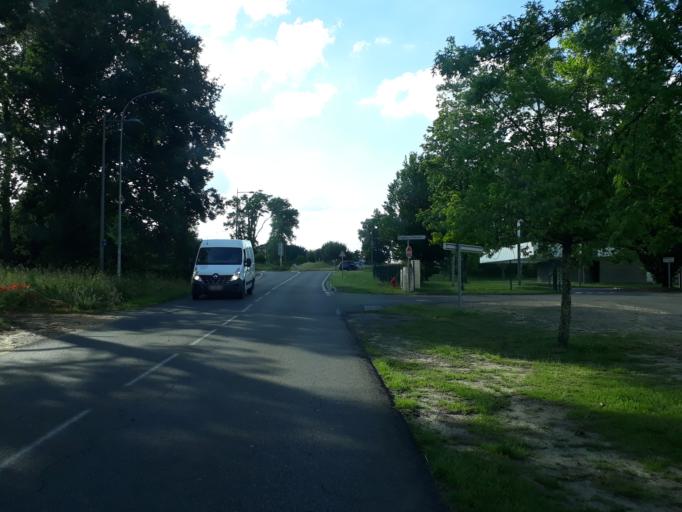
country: FR
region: Aquitaine
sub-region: Departement des Landes
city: Mont-de-Marsan
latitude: 43.9052
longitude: -0.4849
